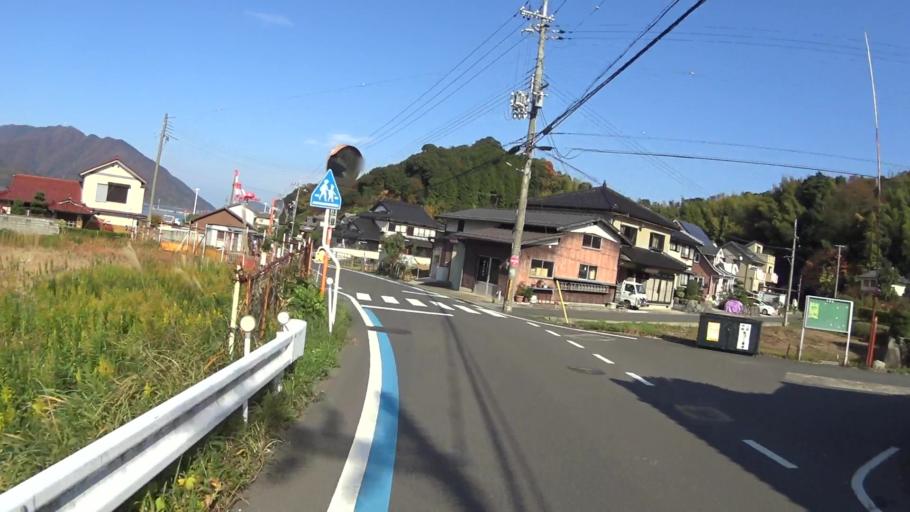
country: JP
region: Kyoto
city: Maizuru
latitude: 35.4635
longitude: 135.3297
